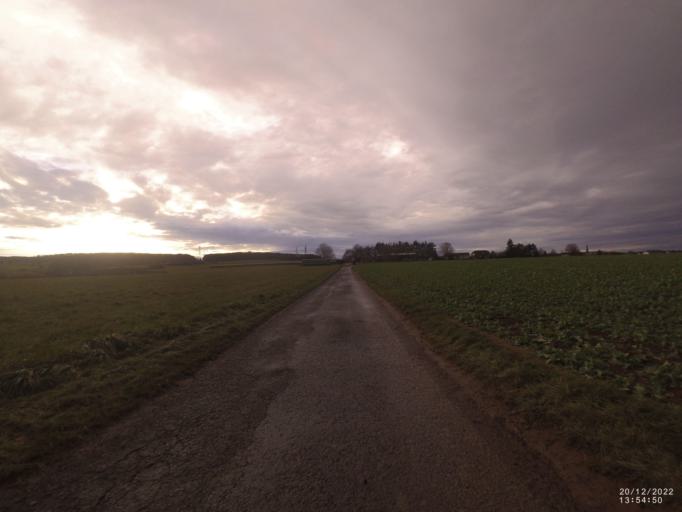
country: DE
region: Rheinland-Pfalz
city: Sinzig
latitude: 50.5275
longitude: 7.2112
